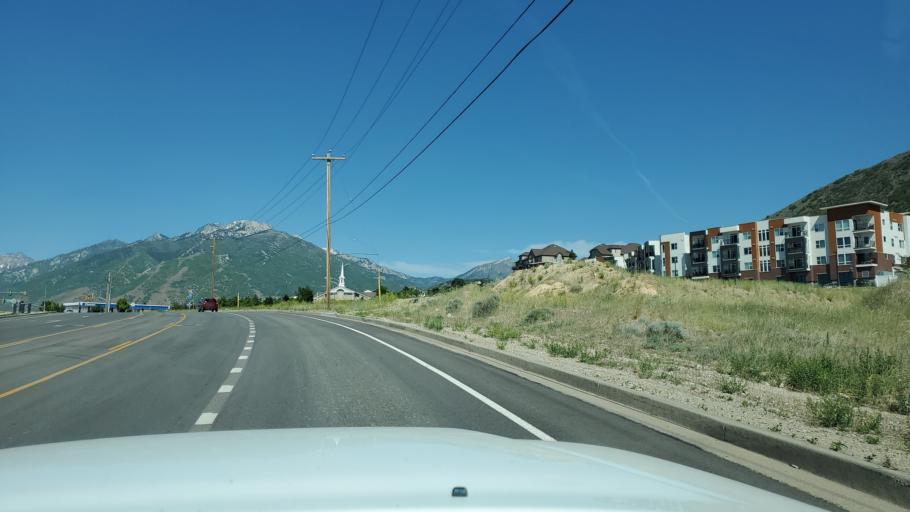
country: US
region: Utah
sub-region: Salt Lake County
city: Draper
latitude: 40.4840
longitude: -111.8863
